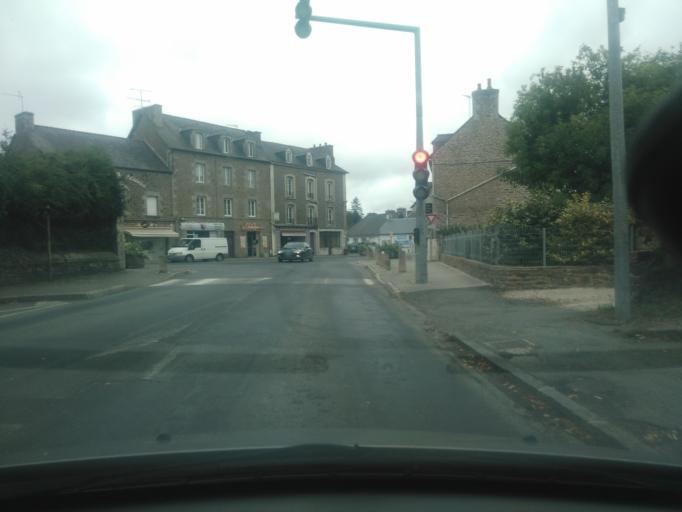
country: FR
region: Brittany
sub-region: Departement des Cotes-d'Armor
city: Lanvallay
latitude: 48.4542
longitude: -2.0266
